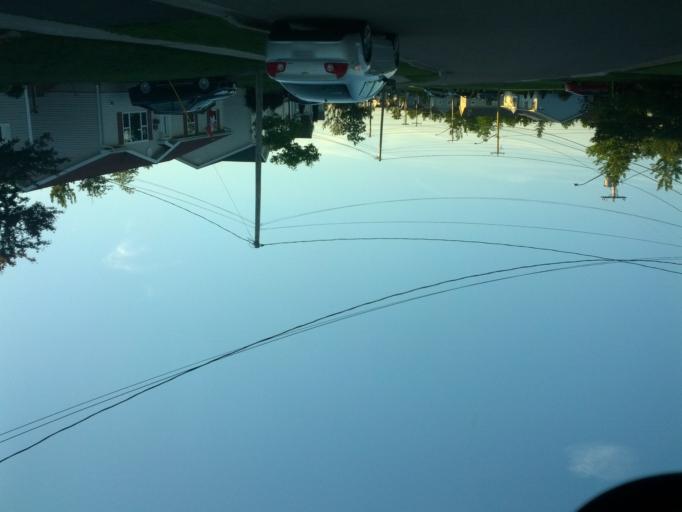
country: CA
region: New Brunswick
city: Moncton
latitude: 46.1186
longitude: -64.8695
